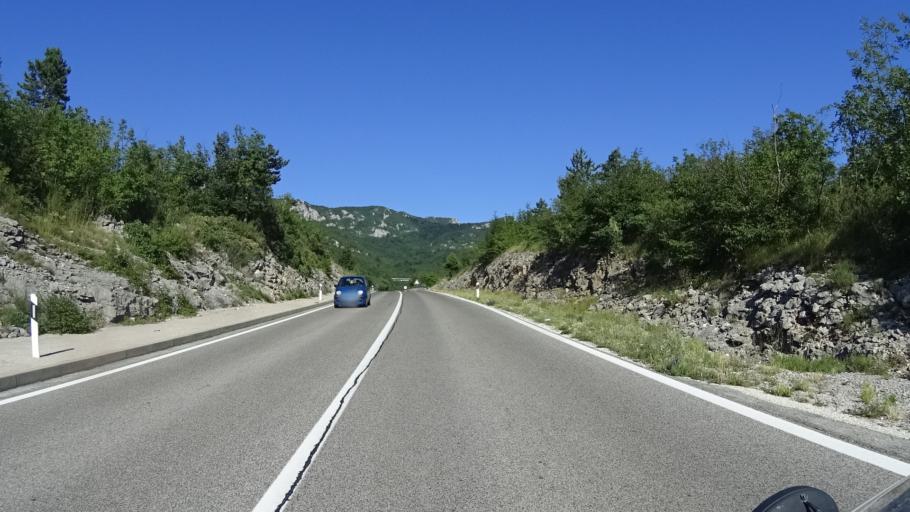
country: HR
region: Istarska
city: Lovran
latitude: 45.3218
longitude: 14.1600
